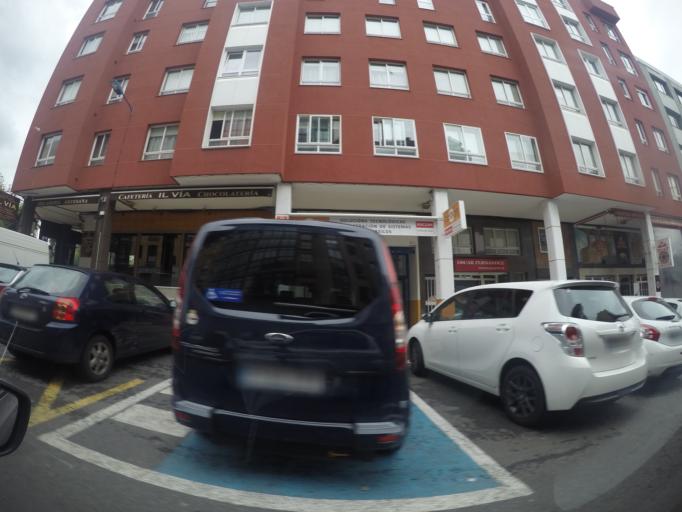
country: ES
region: Galicia
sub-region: Provincia da Coruna
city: Culleredo
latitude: 43.3109
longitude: -8.3826
